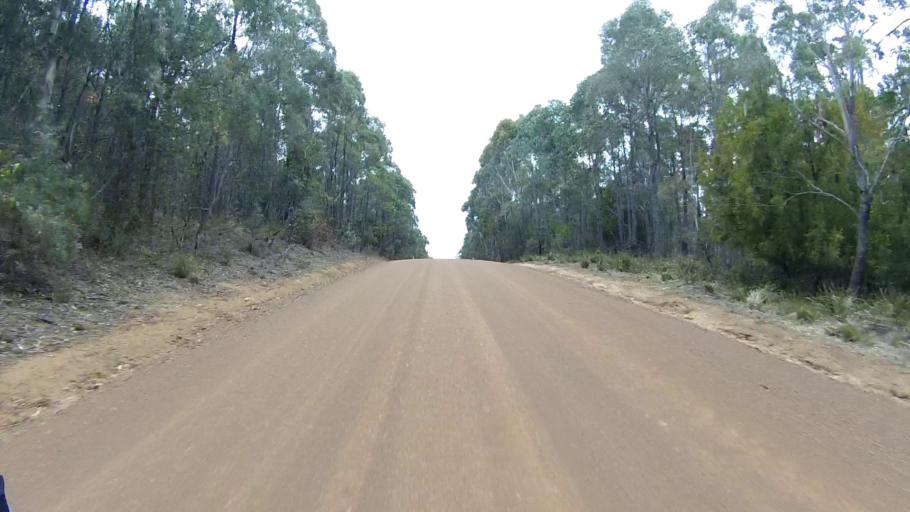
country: AU
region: Tasmania
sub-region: Sorell
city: Sorell
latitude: -42.5962
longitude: 147.8852
